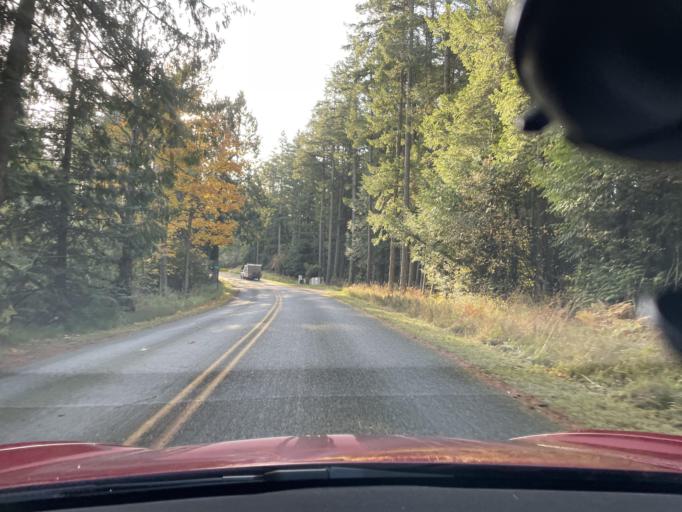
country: US
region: Washington
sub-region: San Juan County
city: Friday Harbor
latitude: 48.5310
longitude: -123.1568
